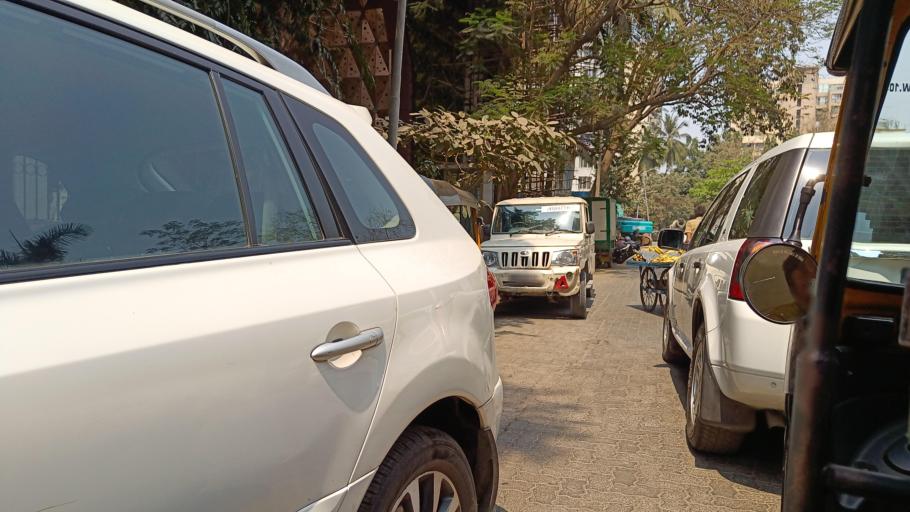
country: IN
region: Maharashtra
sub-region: Mumbai Suburban
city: Mumbai
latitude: 19.1135
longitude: 72.8309
